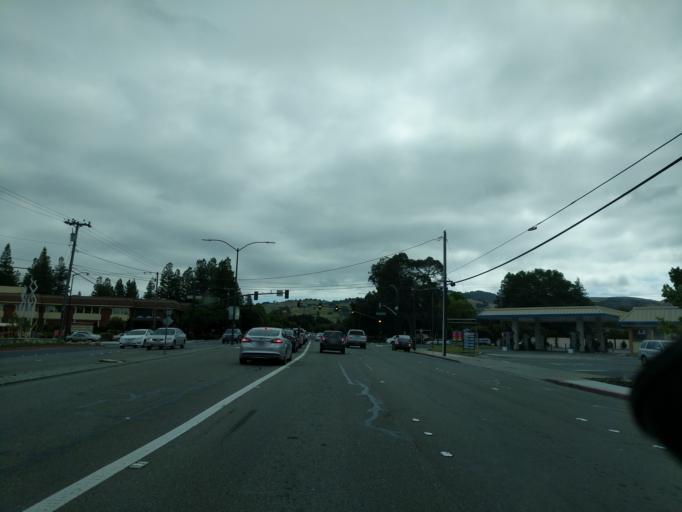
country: US
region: California
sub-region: Contra Costa County
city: Waldon
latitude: 37.9264
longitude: -122.0172
